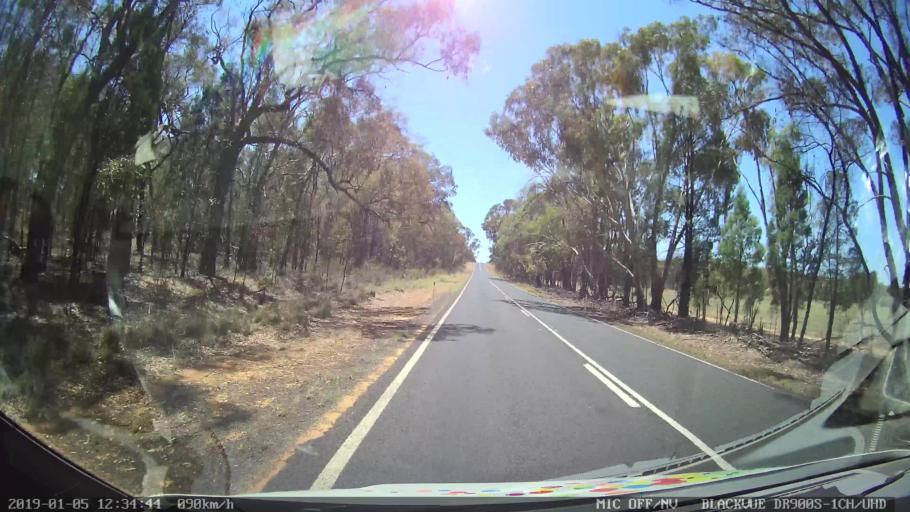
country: AU
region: New South Wales
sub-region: Warrumbungle Shire
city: Coonabarabran
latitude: -31.2114
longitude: 149.4148
